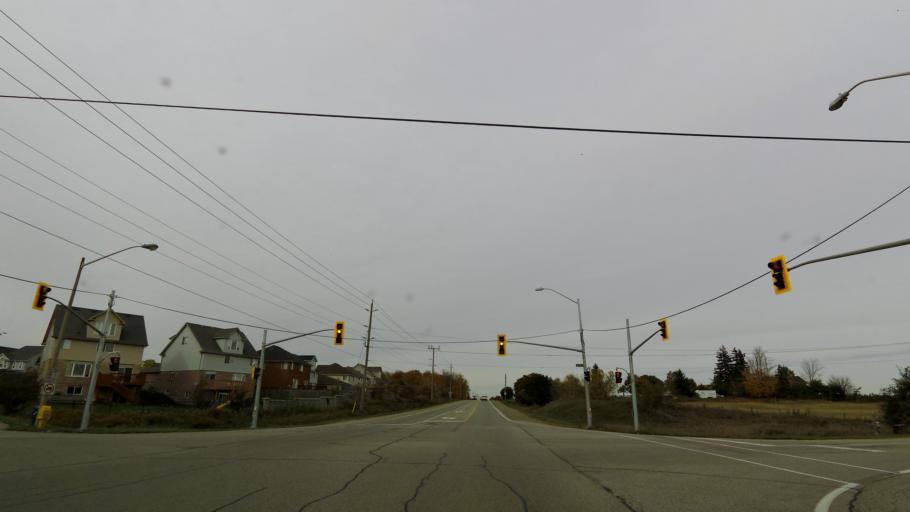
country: CA
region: Ontario
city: Cambridge
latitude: 43.4294
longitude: -80.2866
